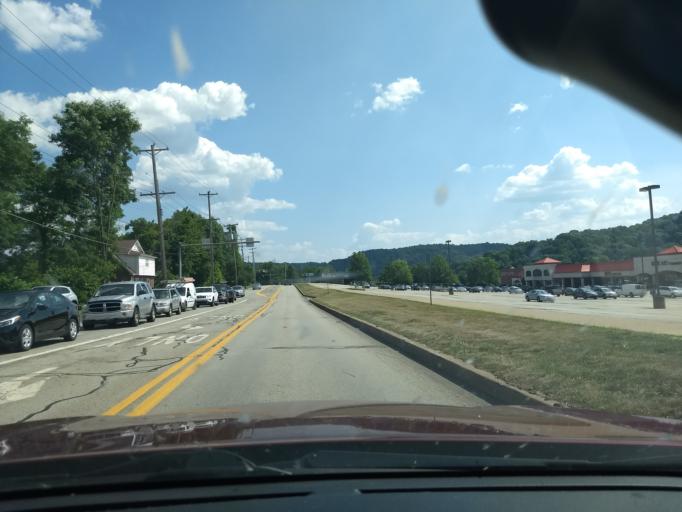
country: US
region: Pennsylvania
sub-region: Westmoreland County
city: Trafford
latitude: 40.3909
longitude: -79.7661
